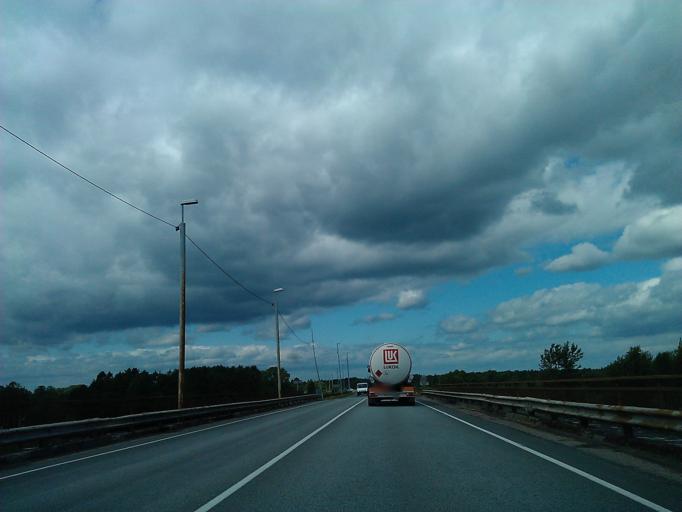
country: LV
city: Tireli
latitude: 56.9307
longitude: 23.6105
